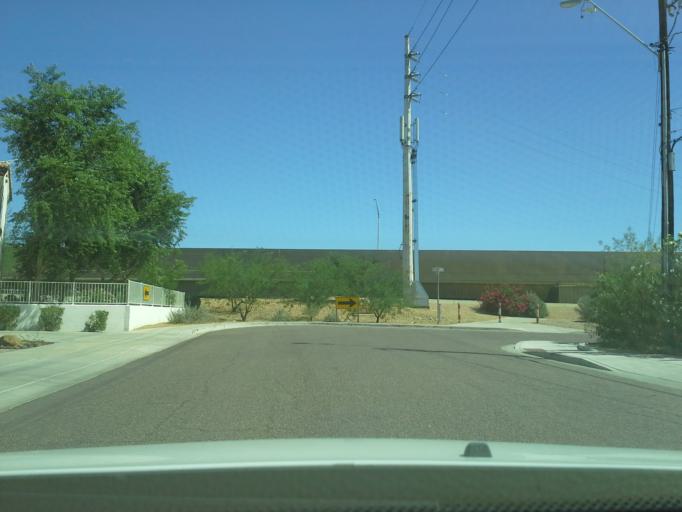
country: US
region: Arizona
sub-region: Maricopa County
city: Phoenix
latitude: 33.5347
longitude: -112.0427
